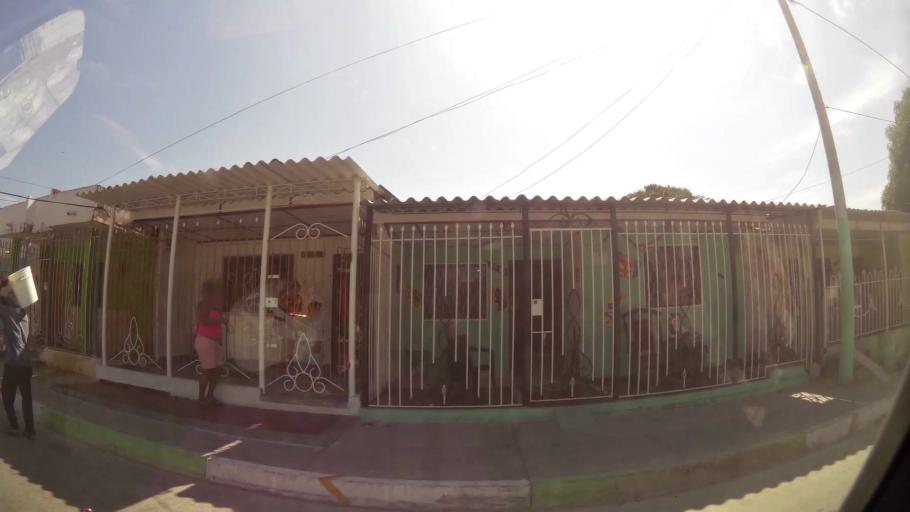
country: CO
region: Atlantico
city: Barranquilla
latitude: 10.9444
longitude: -74.8228
